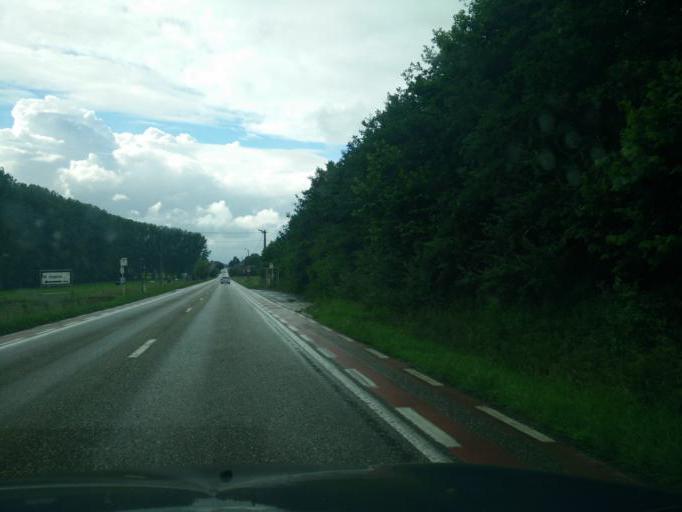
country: BE
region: Flanders
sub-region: Provincie Vlaams-Brabant
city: Gooik
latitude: 50.7866
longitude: 4.0813
